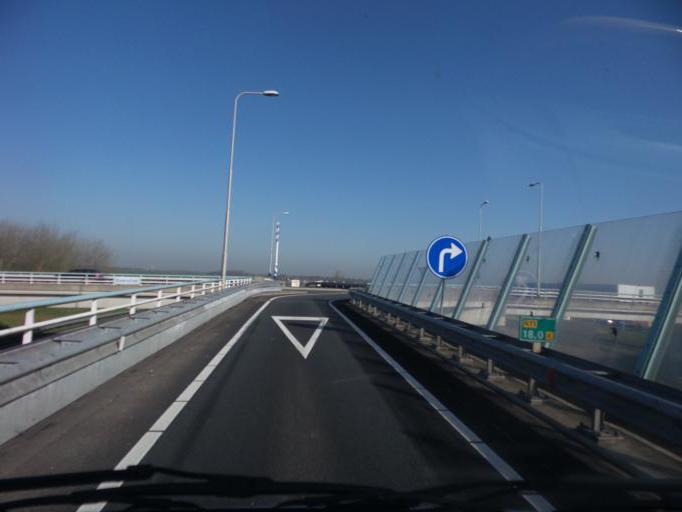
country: NL
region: South Holland
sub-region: Bodegraven-Reeuwijk
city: Bodegraven
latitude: 52.0874
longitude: 4.7347
